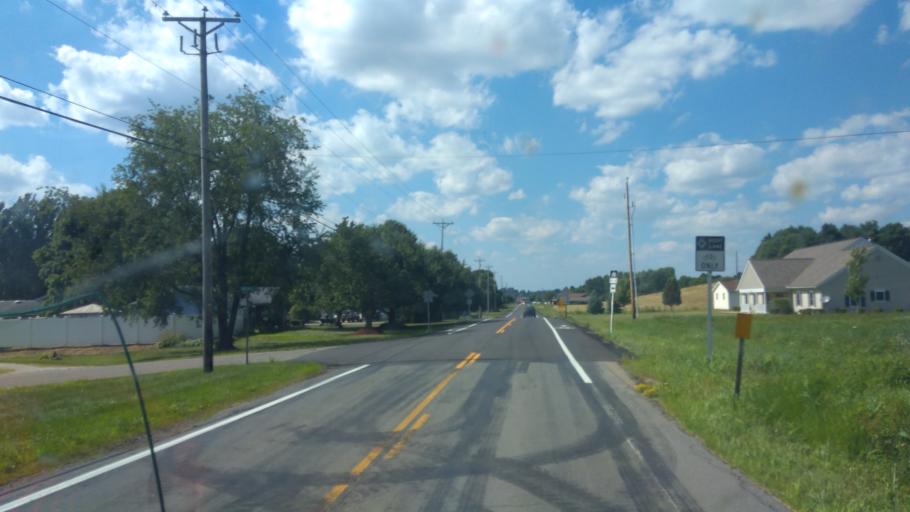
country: US
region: Ohio
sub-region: Tuscarawas County
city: Strasburg
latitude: 40.6236
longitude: -81.4341
